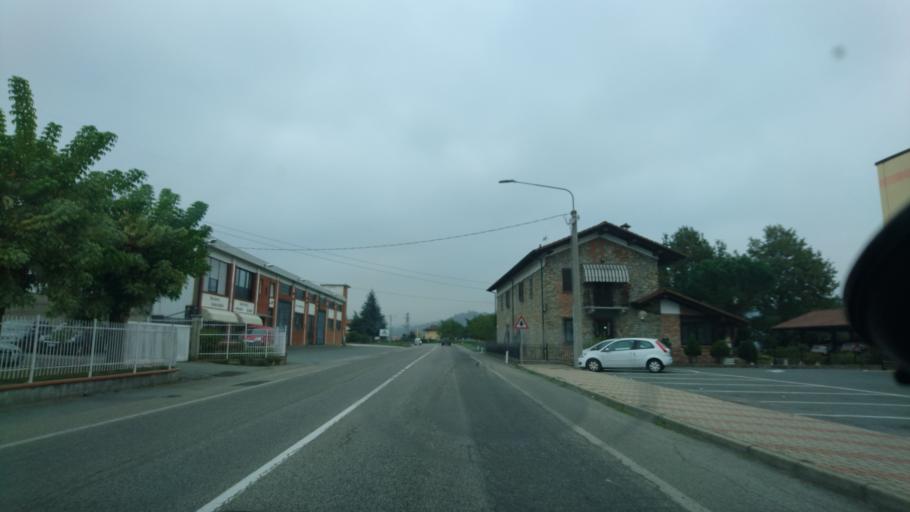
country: IT
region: Piedmont
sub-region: Provincia di Alessandria
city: Bistagno
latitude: 44.6585
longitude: 8.3768
